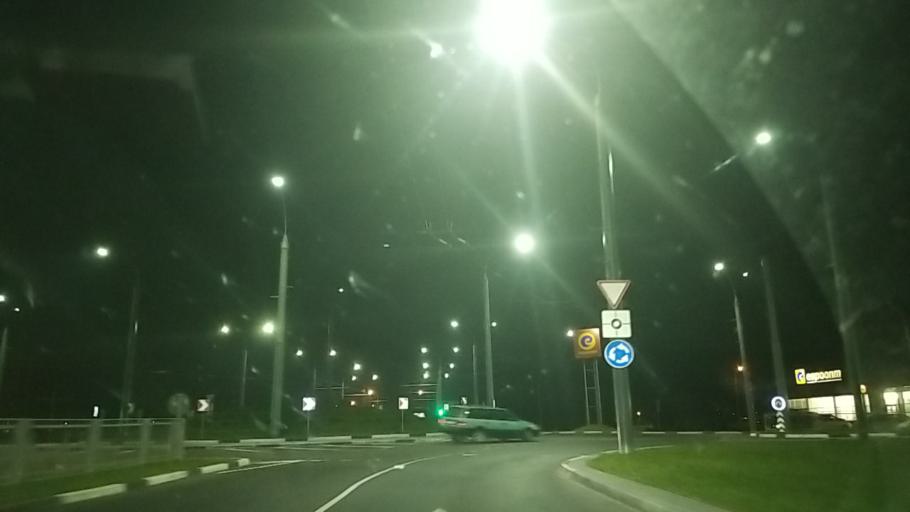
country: BY
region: Brest
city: Brest
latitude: 52.0768
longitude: 23.7681
